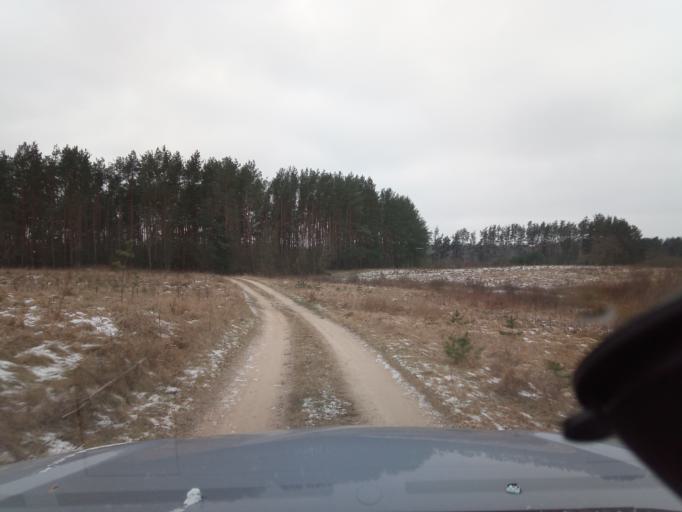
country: LT
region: Alytaus apskritis
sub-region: Alytaus rajonas
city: Daugai
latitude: 54.3762
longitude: 24.4294
